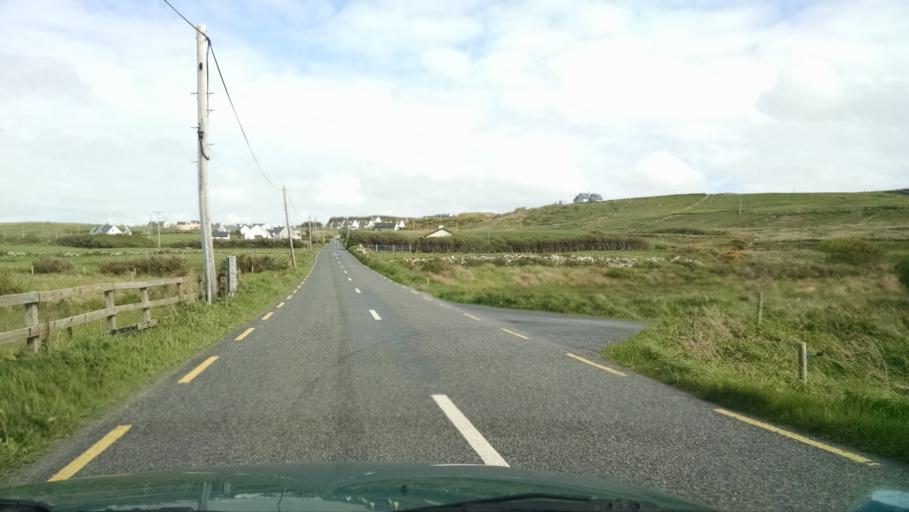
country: IE
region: Connaught
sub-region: County Galway
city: Bearna
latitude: 53.0111
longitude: -9.3653
